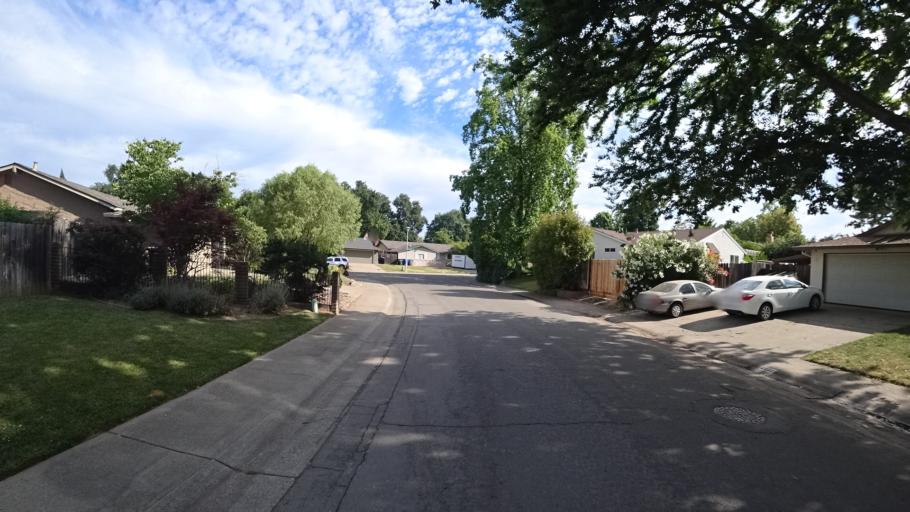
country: US
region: California
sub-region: Sacramento County
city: Rosemont
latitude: 38.5625
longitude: -121.3897
